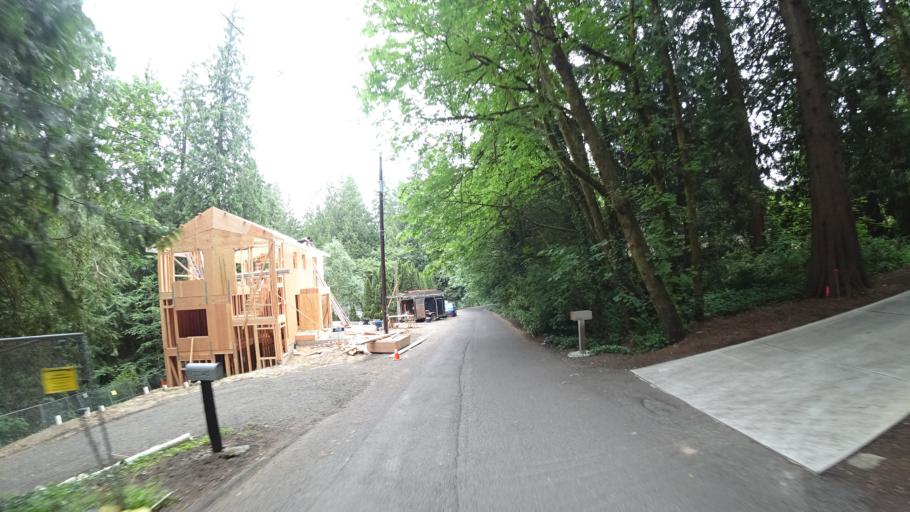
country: US
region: Oregon
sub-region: Clackamas County
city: Lake Oswego
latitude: 45.4437
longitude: -122.7117
